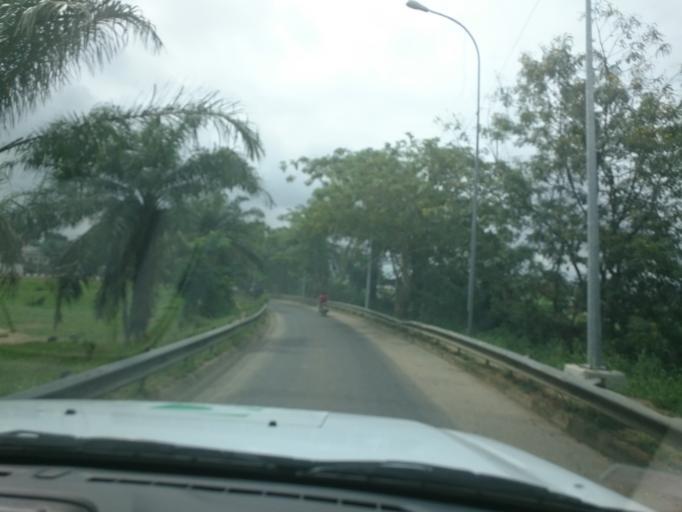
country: CM
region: Littoral
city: Douala
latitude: 4.0157
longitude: 9.6994
